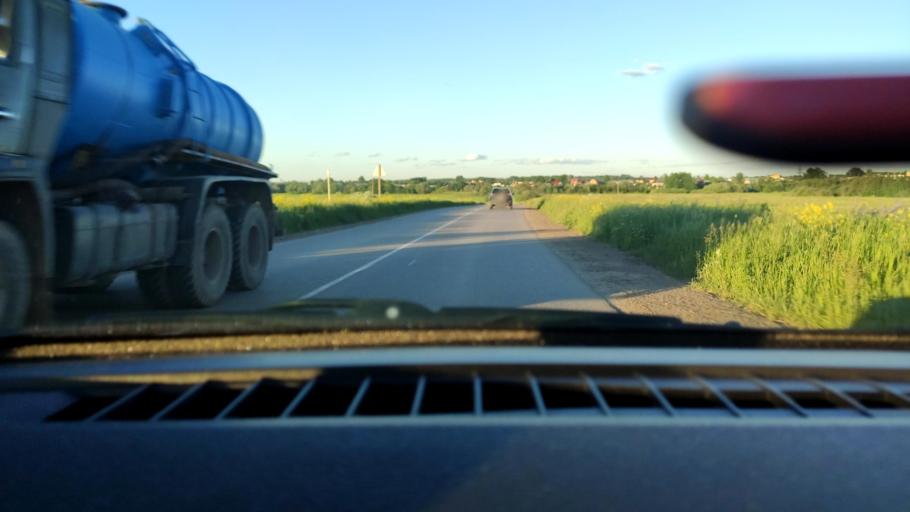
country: RU
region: Perm
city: Kultayevo
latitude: 57.9278
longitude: 55.9890
